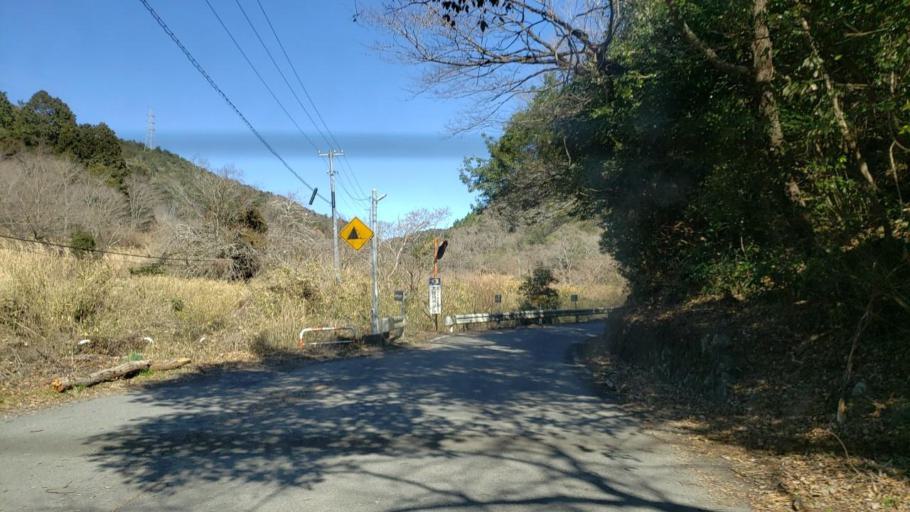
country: JP
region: Tokushima
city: Narutocho-mitsuishi
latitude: 34.1780
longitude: 134.5470
